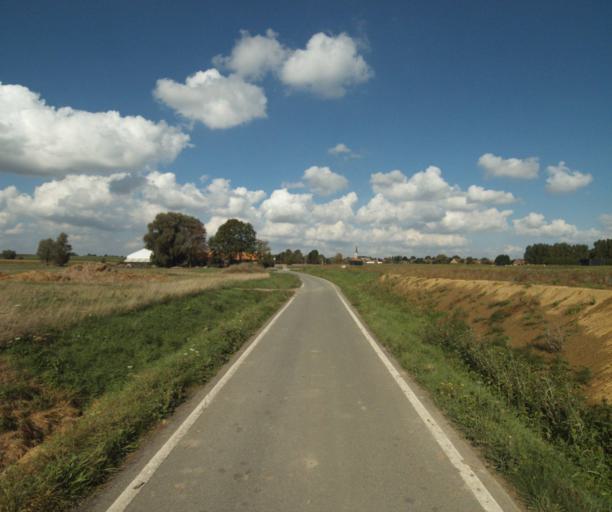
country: FR
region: Nord-Pas-de-Calais
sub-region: Departement du Nord
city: Herlies
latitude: 50.5698
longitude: 2.8486
